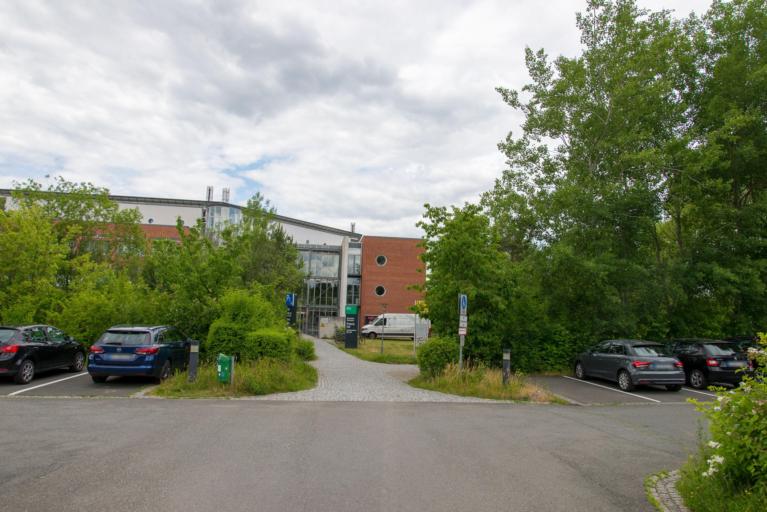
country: DE
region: Bavaria
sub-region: Upper Franconia
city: Bayreuth
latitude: 49.9271
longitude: 11.5867
